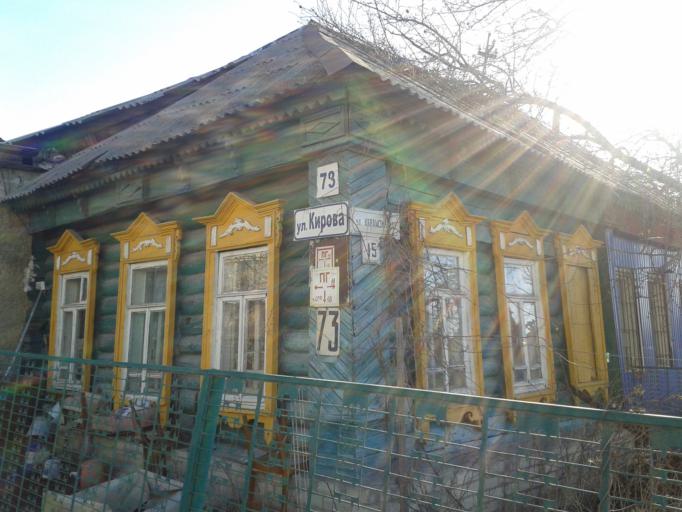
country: RU
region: Ulyanovsk
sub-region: Ulyanovskiy Rayon
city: Ulyanovsk
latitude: 54.2963
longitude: 48.3776
